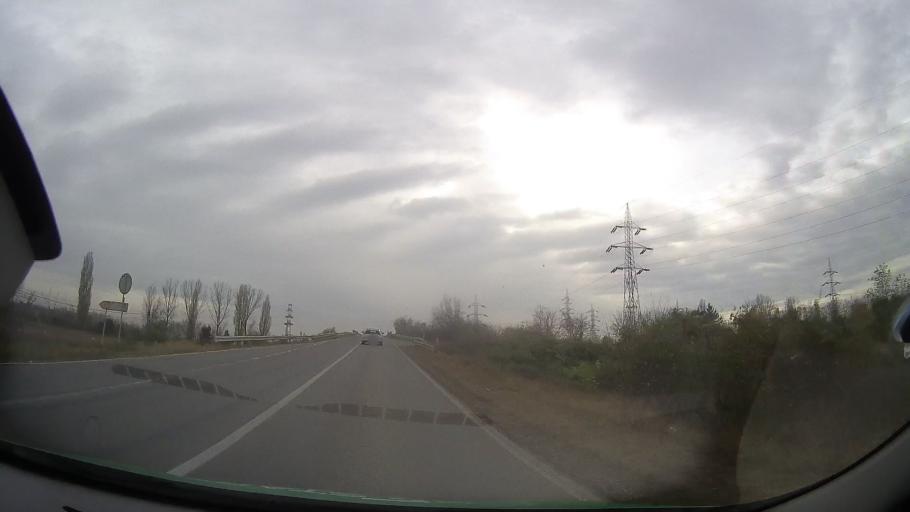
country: RO
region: Prahova
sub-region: Comuna Berceni
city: Berceni
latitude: 44.9424
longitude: 26.1012
